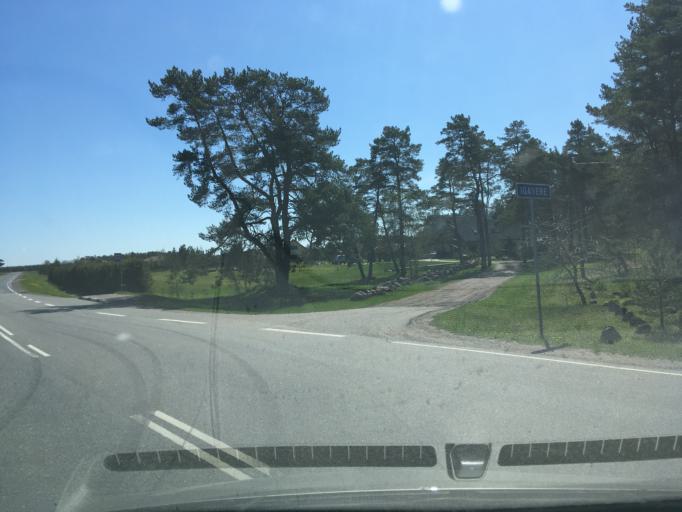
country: EE
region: Harju
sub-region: Raasiku vald
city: Arukula
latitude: 59.3559
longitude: 25.0757
